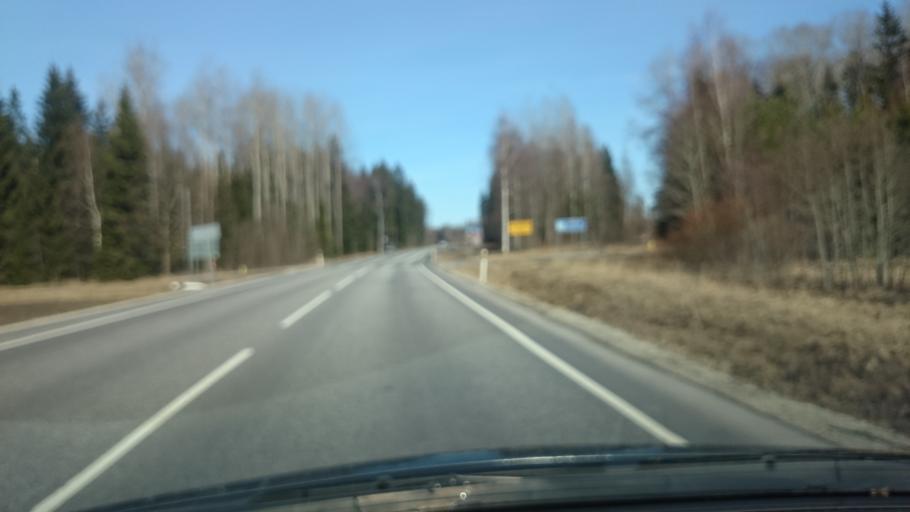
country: EE
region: Jaervamaa
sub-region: Tueri vald
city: Sarevere
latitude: 58.7166
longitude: 25.2736
